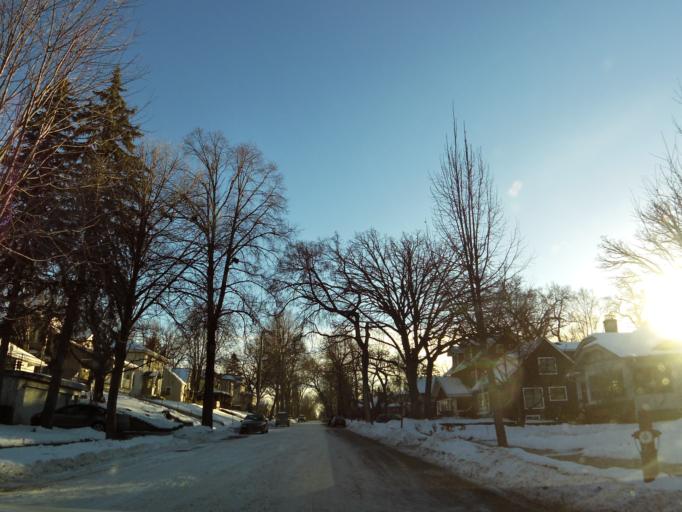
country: US
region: Minnesota
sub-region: Hennepin County
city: Saint Louis Park
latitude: 44.9304
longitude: -93.3227
